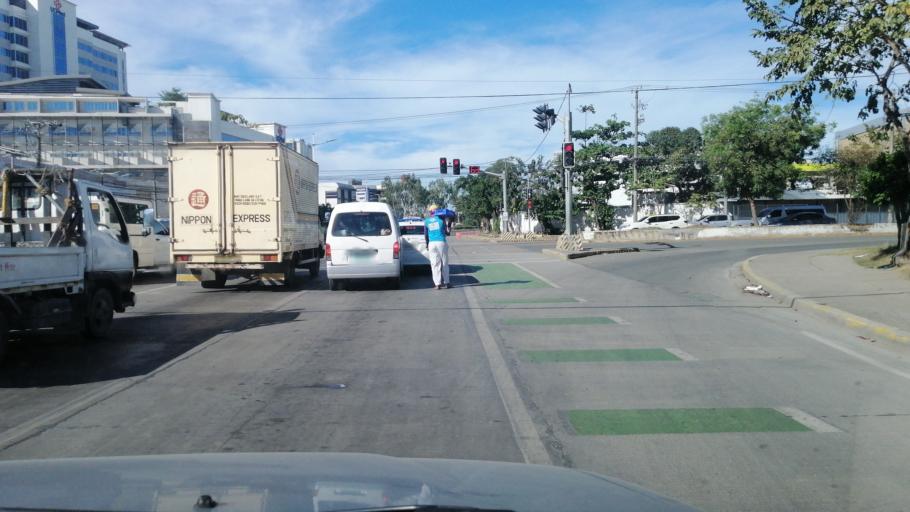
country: PH
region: Central Visayas
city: Mandaue City
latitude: 10.3191
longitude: 123.9306
